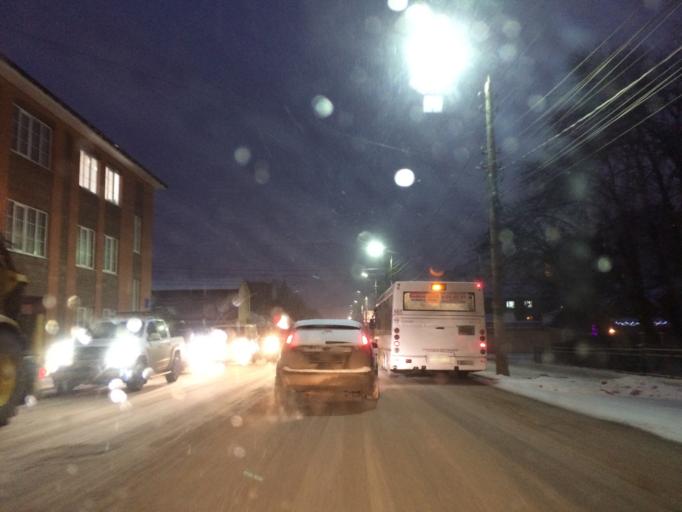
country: RU
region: Tula
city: Tula
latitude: 54.2054
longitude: 37.6534
